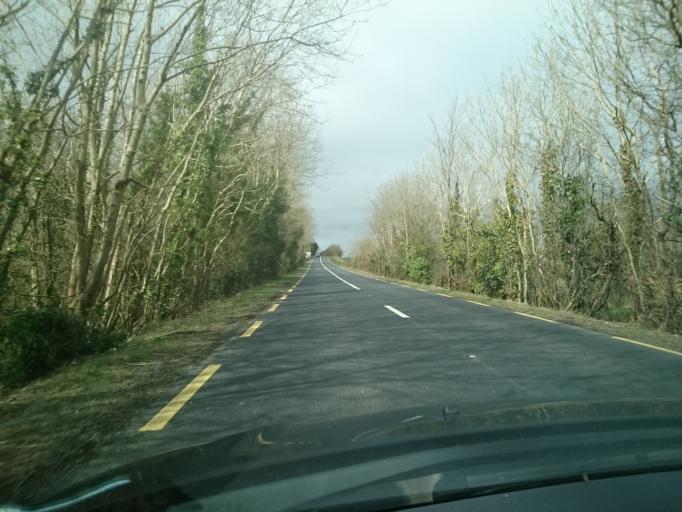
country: IE
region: Connaught
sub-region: Maigh Eo
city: Claremorris
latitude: 53.7693
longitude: -9.0564
